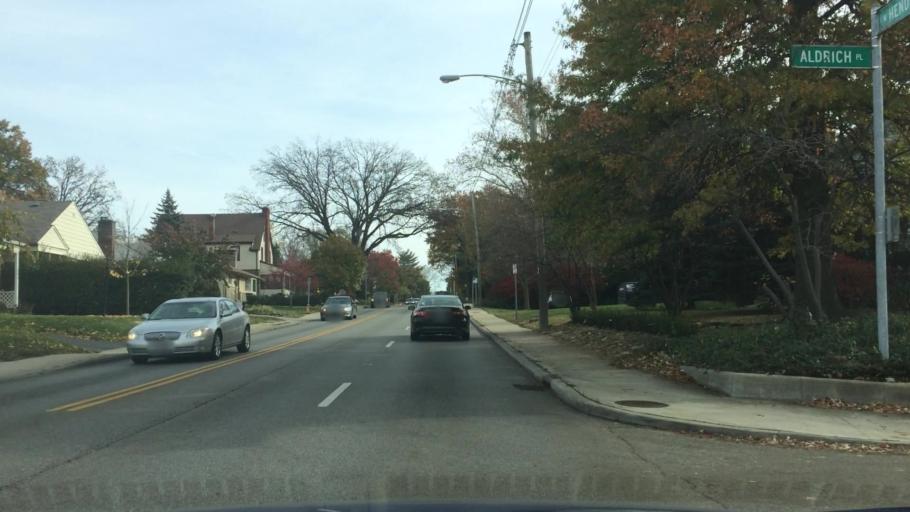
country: US
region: Ohio
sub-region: Franklin County
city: Worthington
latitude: 40.0517
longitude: -83.0260
